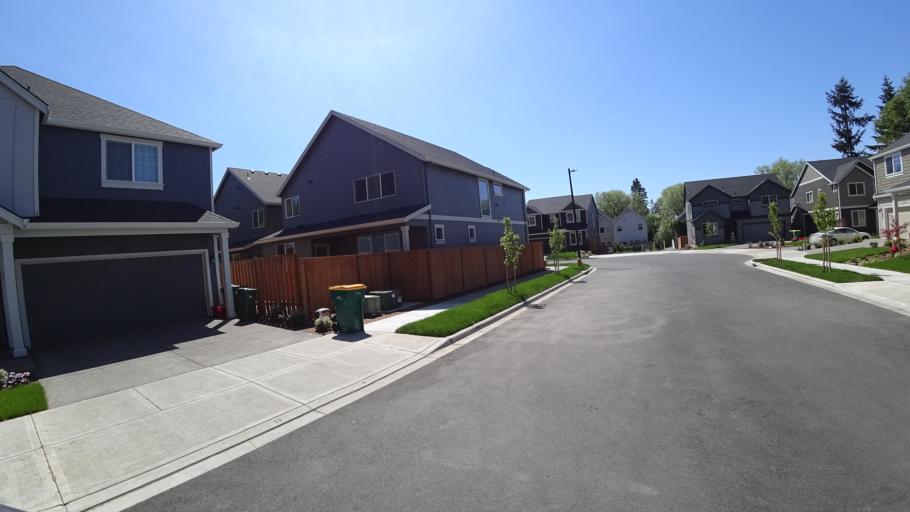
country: US
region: Oregon
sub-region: Washington County
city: Aloha
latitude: 45.4820
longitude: -122.8441
